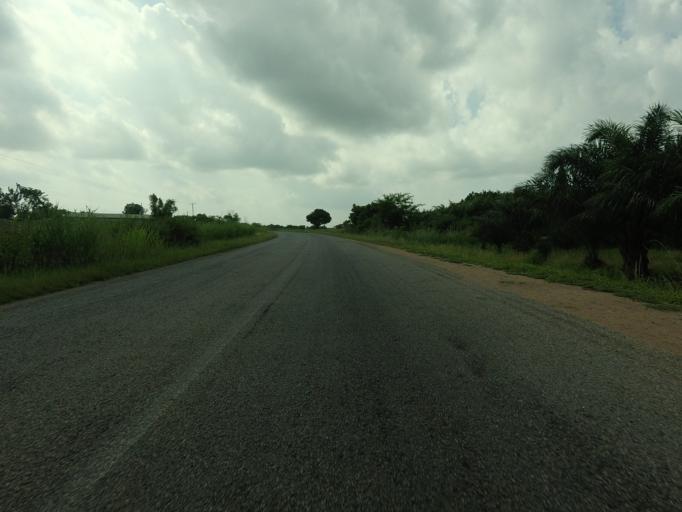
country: GH
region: Volta
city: Ho
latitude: 6.4324
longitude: 0.7322
